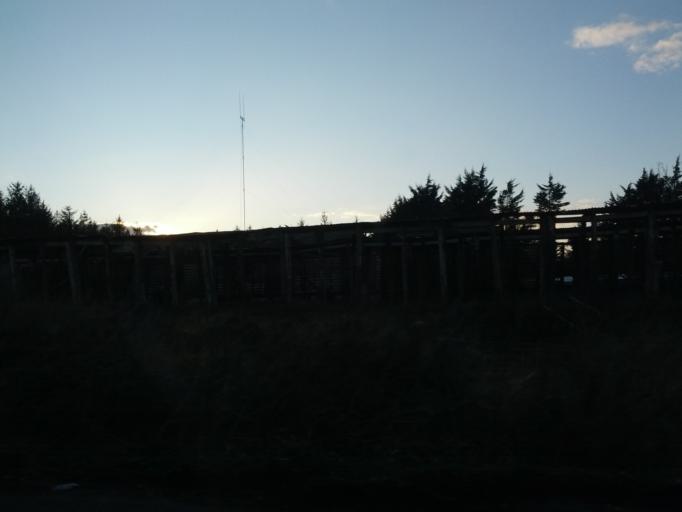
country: IE
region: Connaught
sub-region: County Galway
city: Athenry
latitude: 53.3060
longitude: -8.6217
